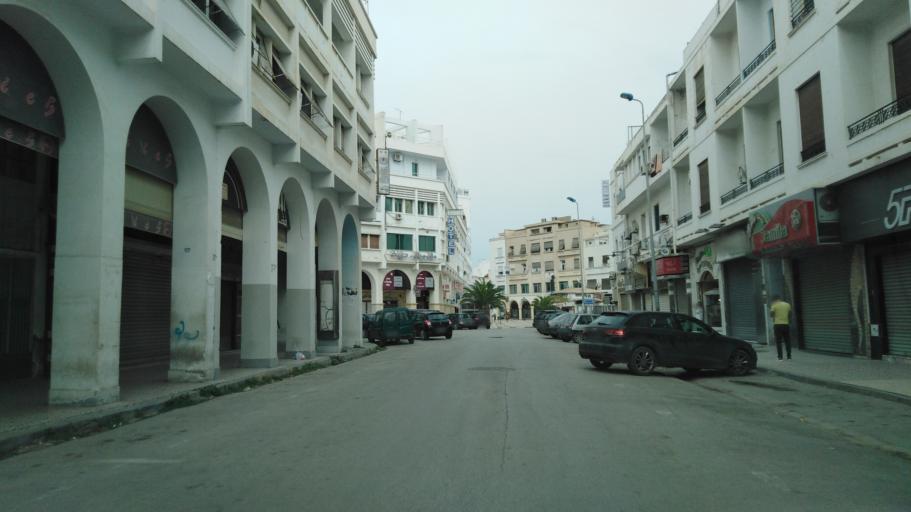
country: TN
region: Safaqis
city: Sfax
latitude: 34.7334
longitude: 10.7617
